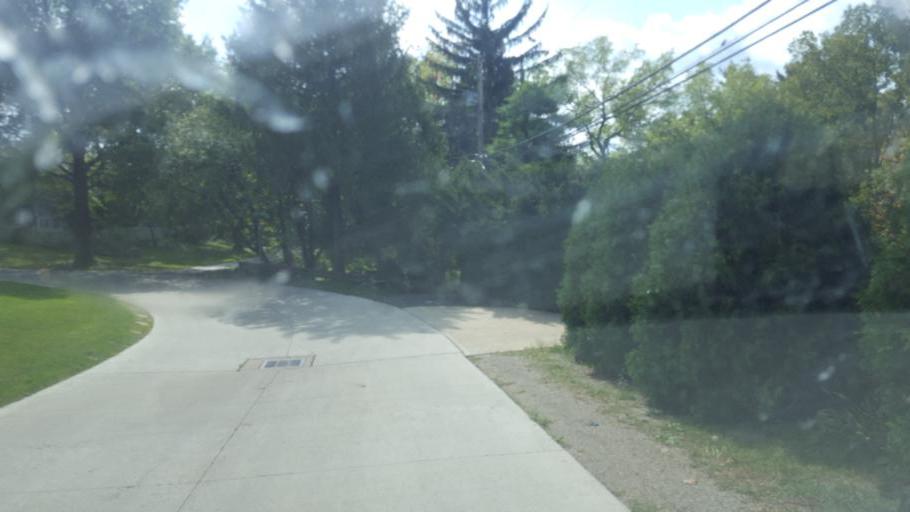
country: US
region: Ohio
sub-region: Franklin County
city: Worthington
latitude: 40.0855
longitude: -83.0116
